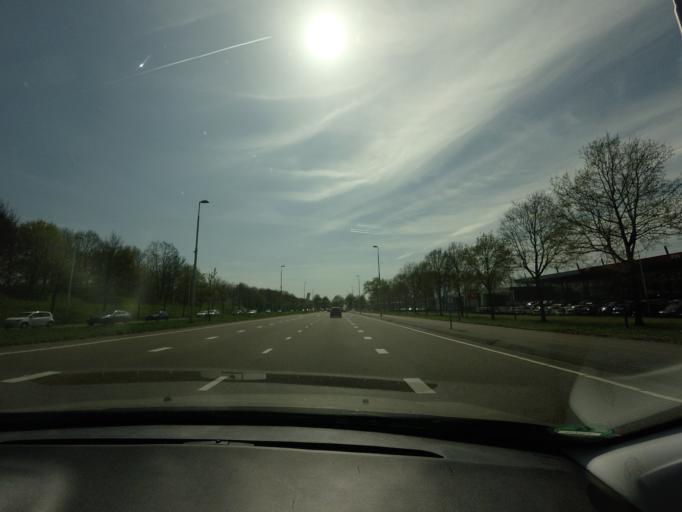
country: NL
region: North Brabant
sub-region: Gemeente Tilburg
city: Tilburg
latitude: 51.5857
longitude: 5.0682
